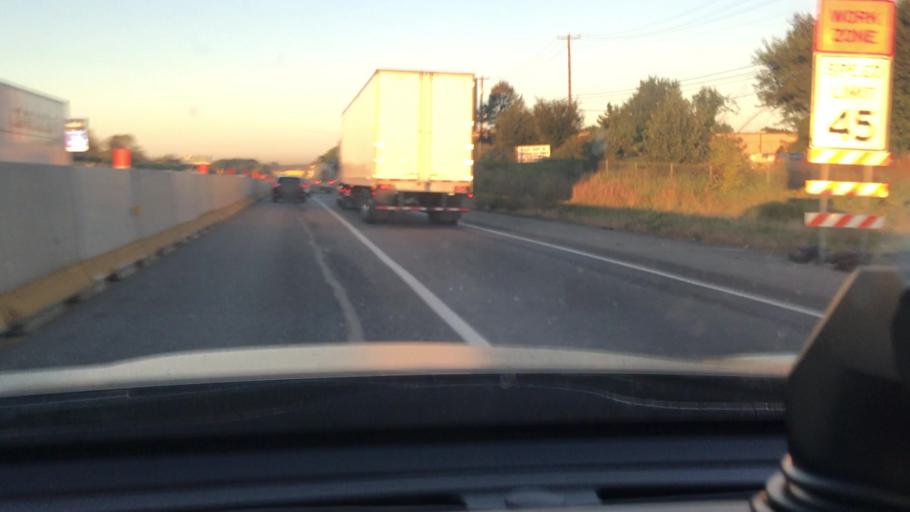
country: US
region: Pennsylvania
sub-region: Lehigh County
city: Fullerton
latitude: 40.6359
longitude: -75.4543
